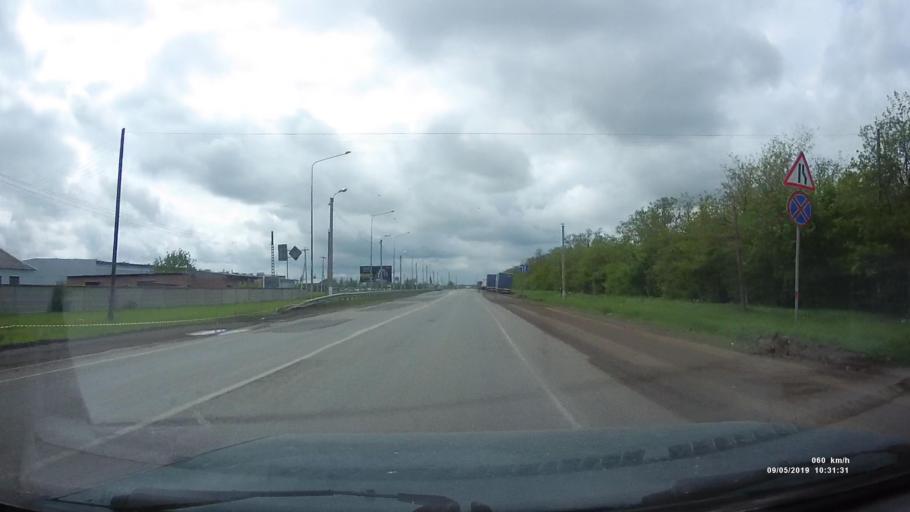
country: RU
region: Rostov
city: Azov
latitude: 47.0808
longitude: 39.4278
